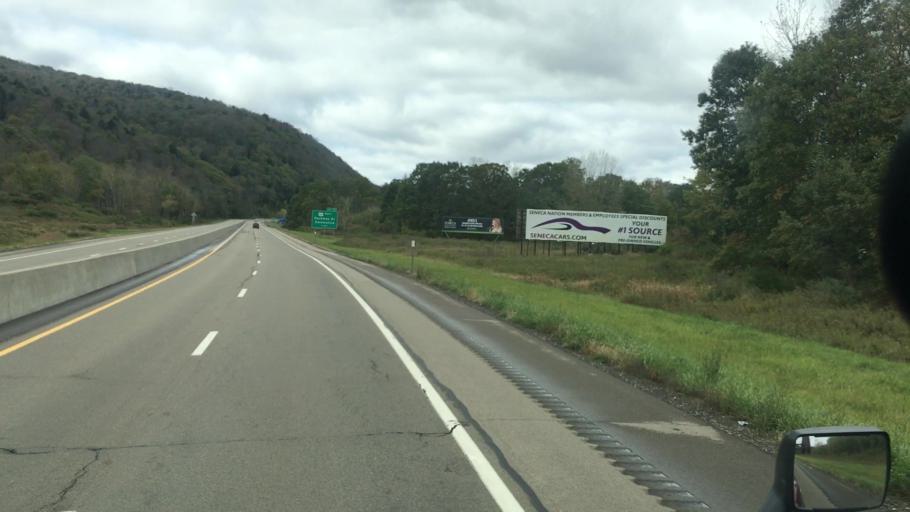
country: US
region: New York
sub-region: Cattaraugus County
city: Salamanca
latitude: 42.1475
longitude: -78.6757
